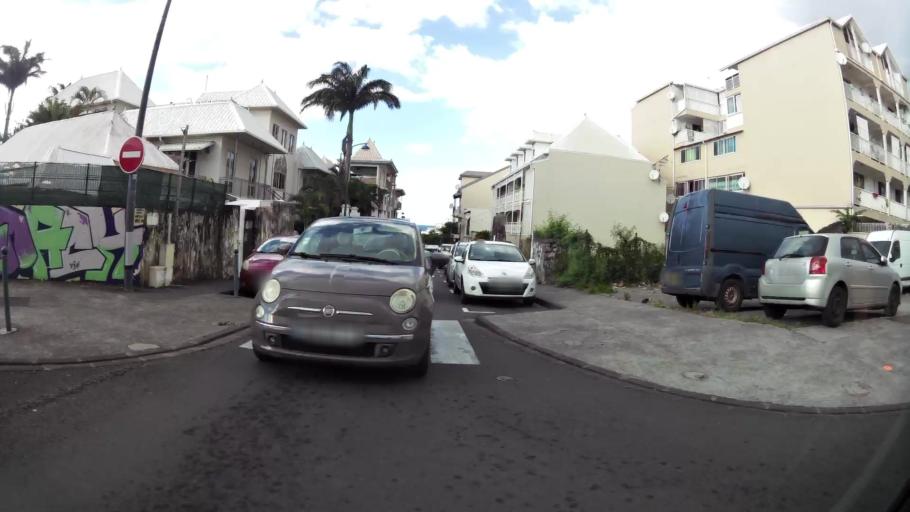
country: RE
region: Reunion
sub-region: Reunion
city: Saint-Denis
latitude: -20.8808
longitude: 55.4548
